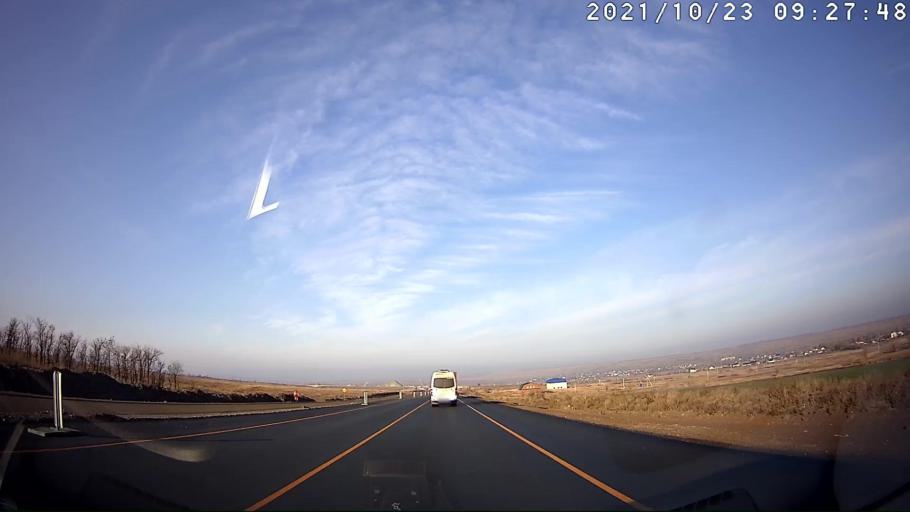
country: RU
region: Saratov
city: Sokolovyy
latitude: 51.6745
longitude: 45.9266
